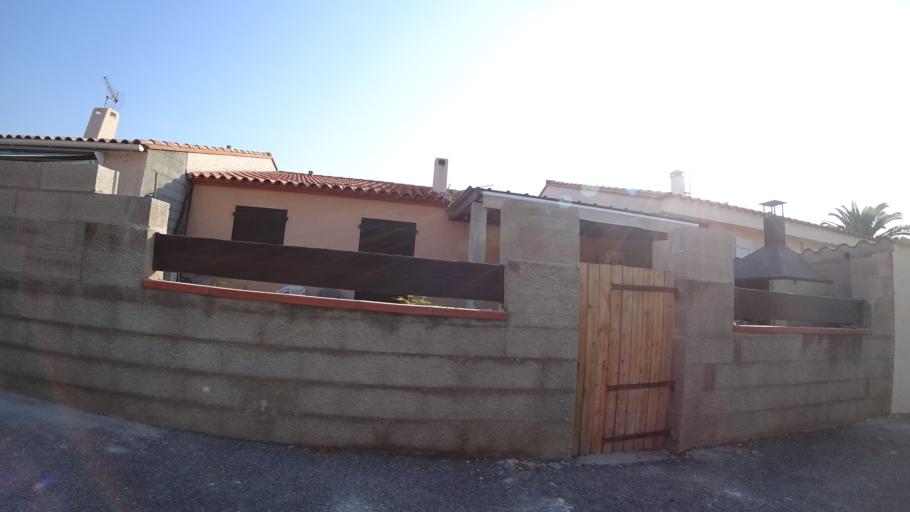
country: FR
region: Languedoc-Roussillon
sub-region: Departement des Pyrenees-Orientales
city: Sainte-Marie-Plage
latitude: 42.7284
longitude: 3.0182
